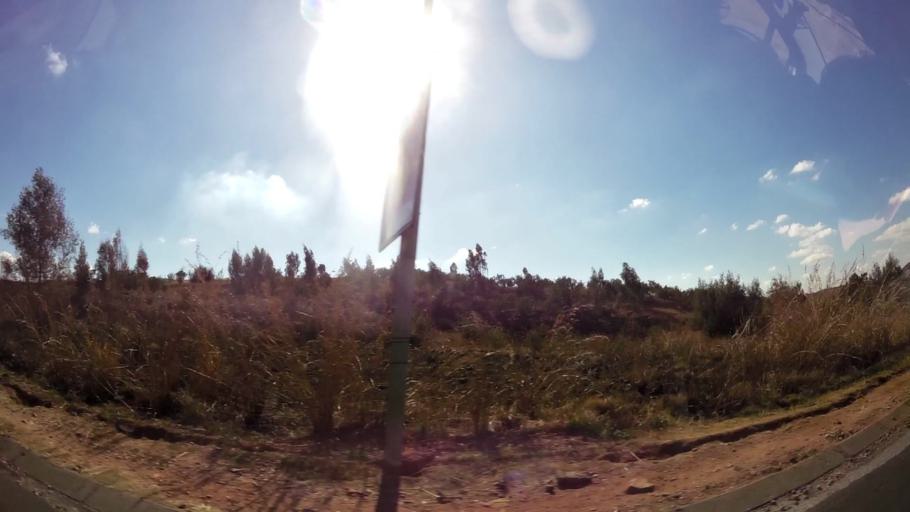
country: ZA
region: Gauteng
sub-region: West Rand District Municipality
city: Krugersdorp
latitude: -26.0922
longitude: 27.8246
